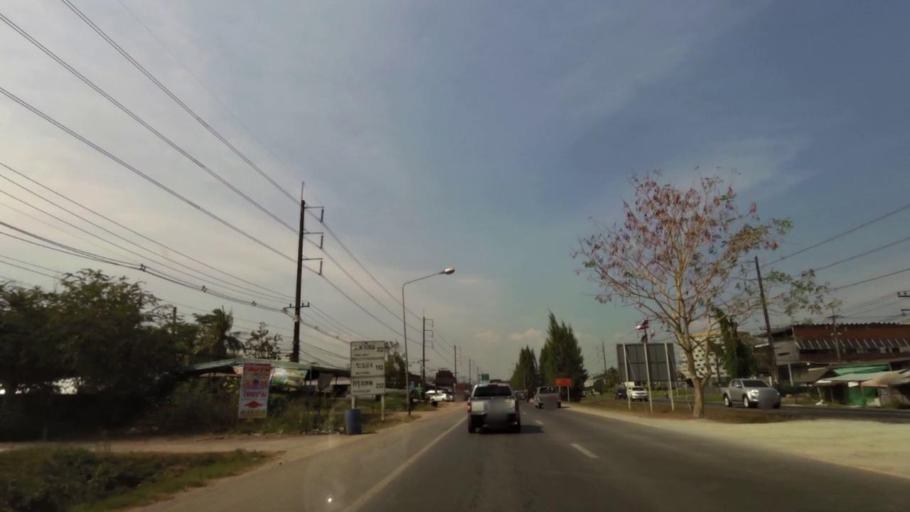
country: TH
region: Chanthaburi
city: Chanthaburi
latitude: 12.6254
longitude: 102.1502
